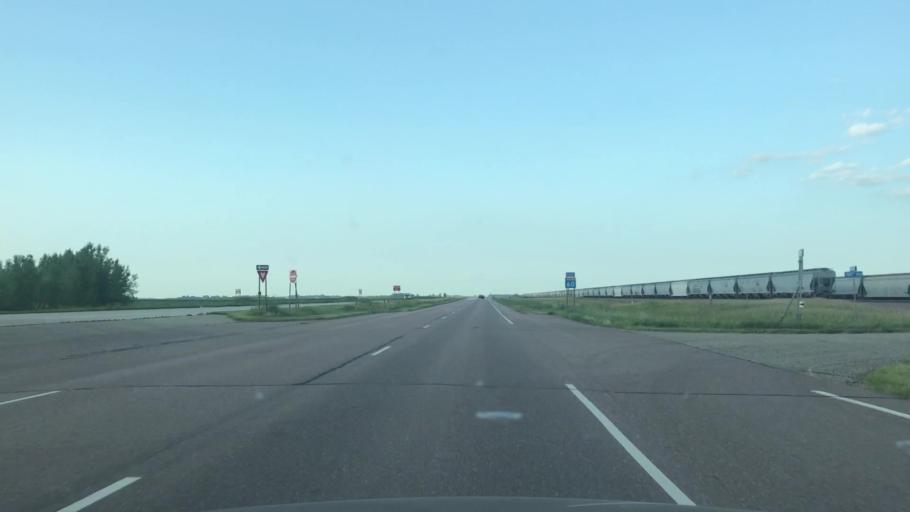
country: US
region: Minnesota
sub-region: Nobles County
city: Worthington
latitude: 43.7213
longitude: -95.4364
